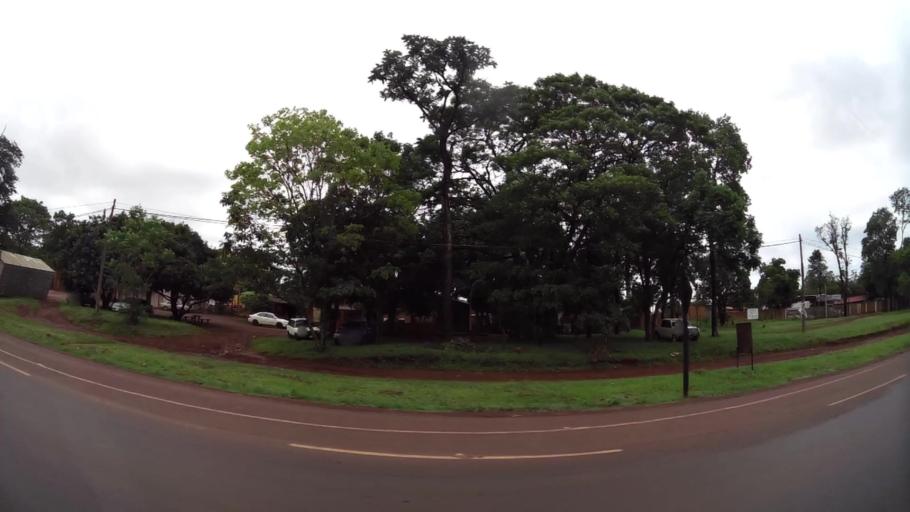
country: PY
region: Alto Parana
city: Ciudad del Este
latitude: -25.4934
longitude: -54.7188
